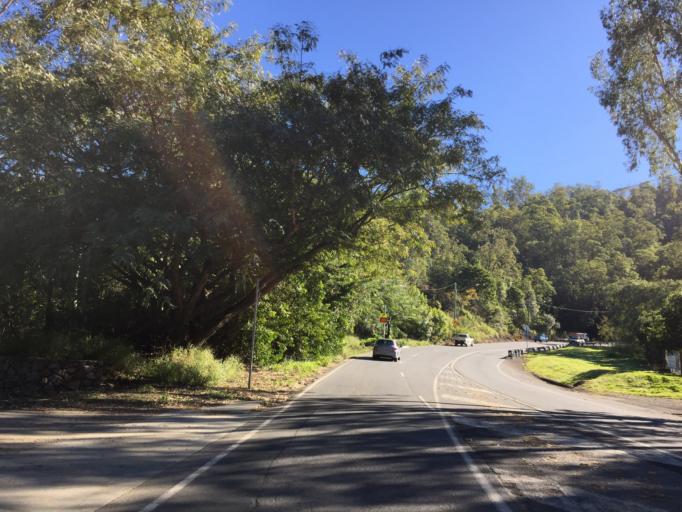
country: AU
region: Queensland
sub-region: Moreton Bay
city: Ferny Hills
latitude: -27.4291
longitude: 152.9430
